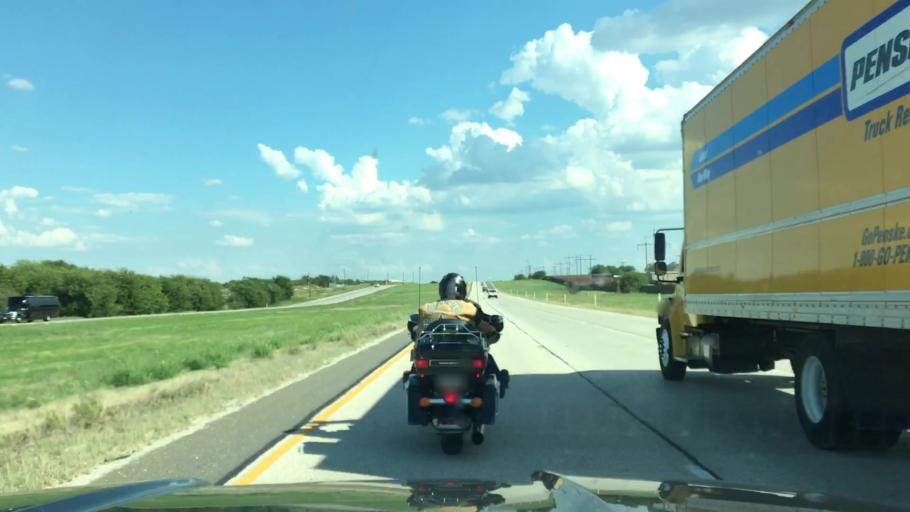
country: US
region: Texas
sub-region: Wise County
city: Decatur
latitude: 33.1735
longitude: -97.5414
